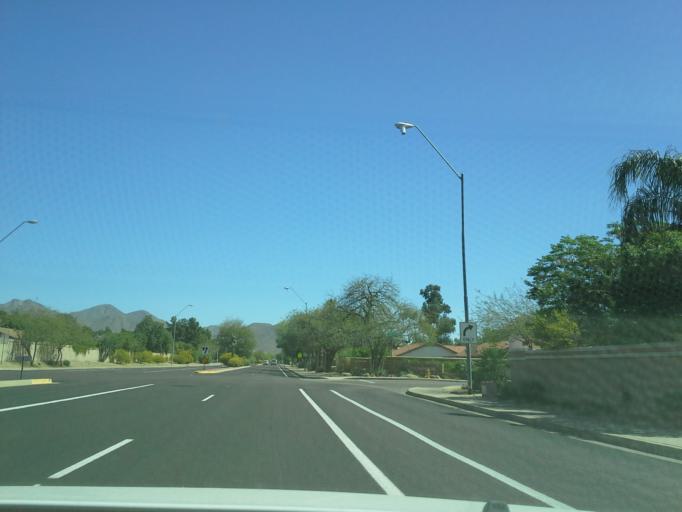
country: US
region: Arizona
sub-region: Maricopa County
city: Paradise Valley
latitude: 33.6115
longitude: -111.8876
